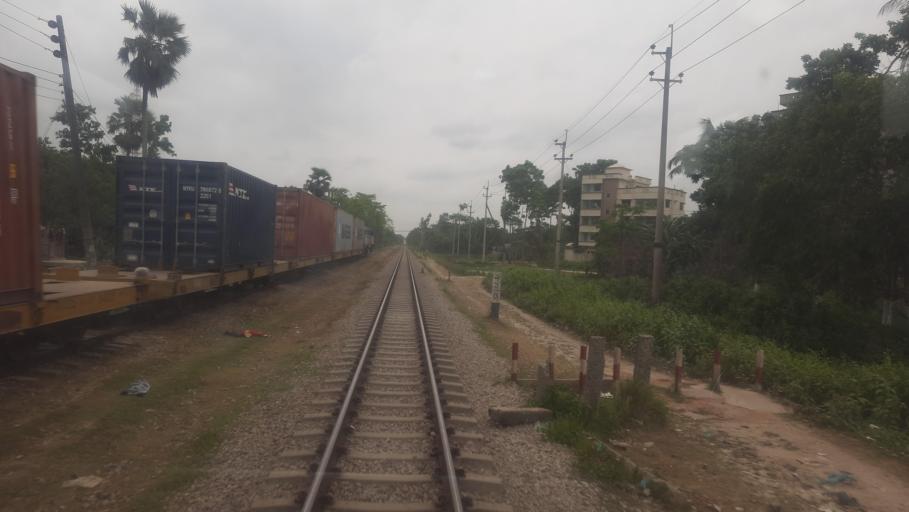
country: BD
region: Chittagong
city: Feni
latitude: 23.0215
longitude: 91.3920
